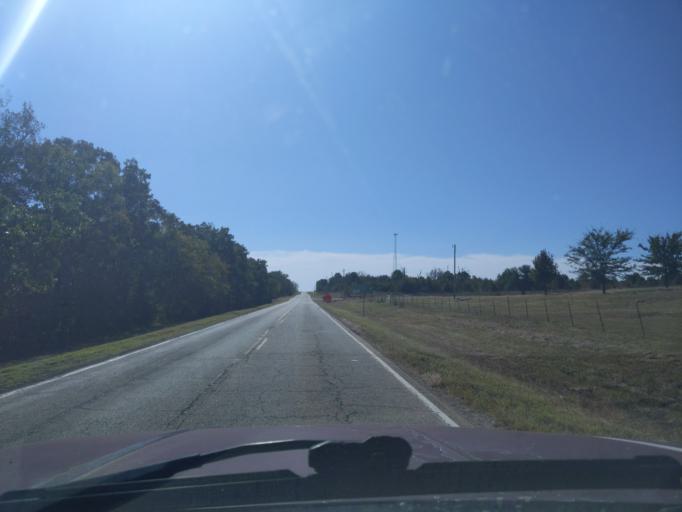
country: US
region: Oklahoma
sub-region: Creek County
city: Bristow
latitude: 35.7281
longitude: -96.3872
